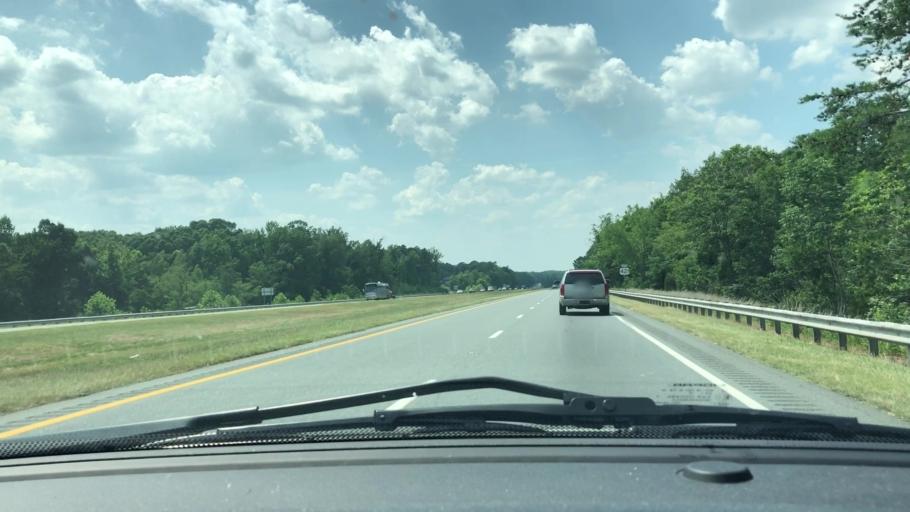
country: US
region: North Carolina
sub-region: Guilford County
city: Forest Oaks
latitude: 35.9679
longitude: -79.7124
